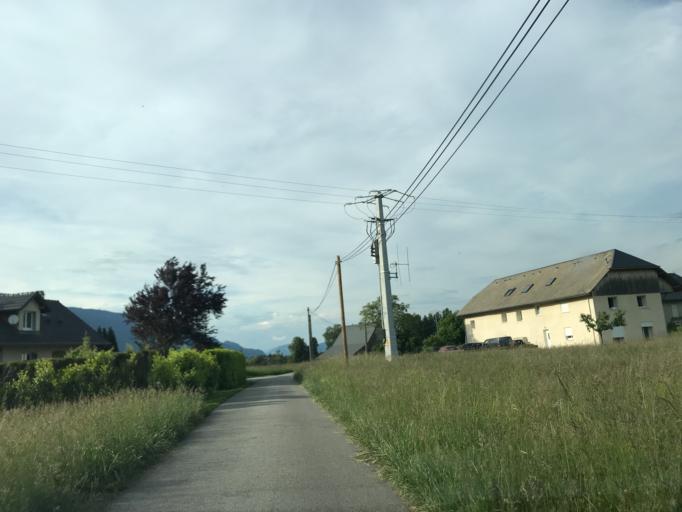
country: FR
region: Rhone-Alpes
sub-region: Departement de la Savoie
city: Vimines
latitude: 45.5630
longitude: 5.8610
